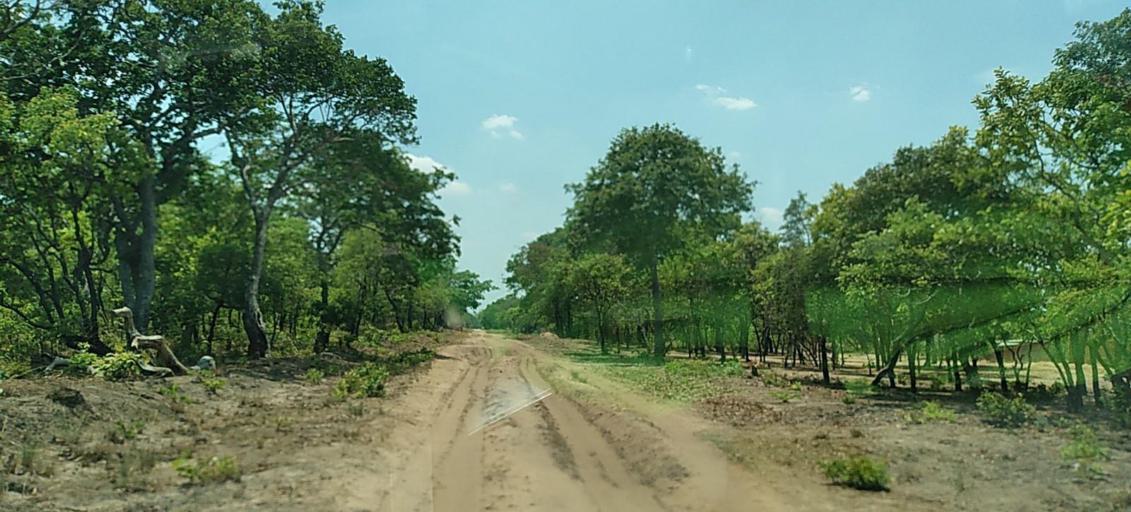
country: CD
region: Katanga
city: Kolwezi
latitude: -11.3826
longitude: 25.2187
